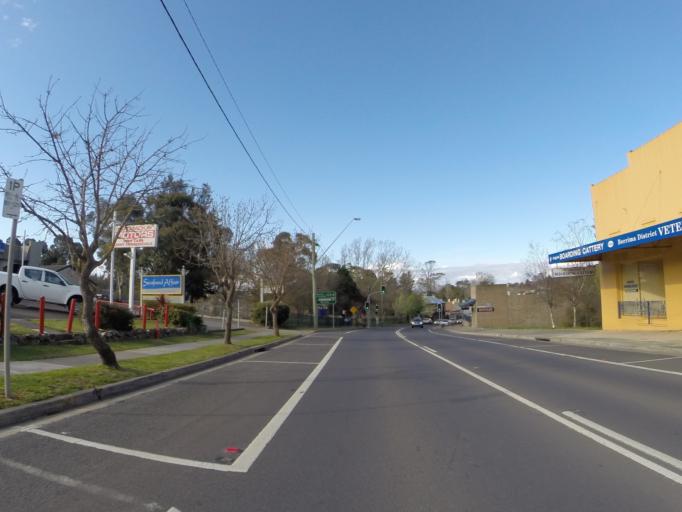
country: AU
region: New South Wales
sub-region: Wingecarribee
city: Moss Vale
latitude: -34.5520
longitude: 150.3667
